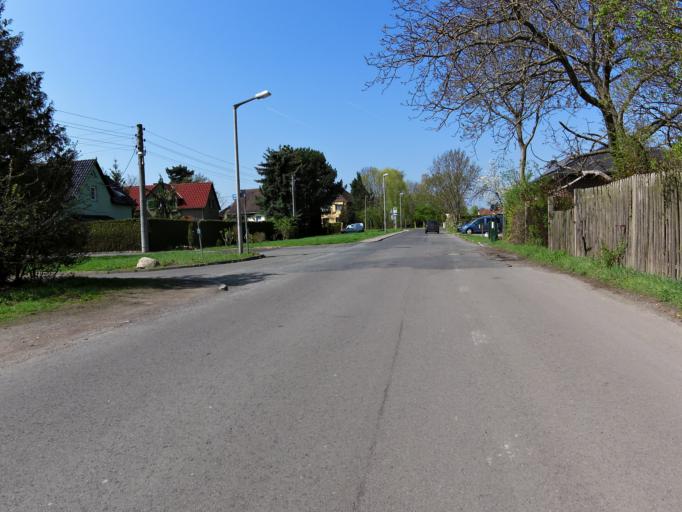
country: DE
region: Saxony
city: Leipzig
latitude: 51.3870
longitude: 12.3269
